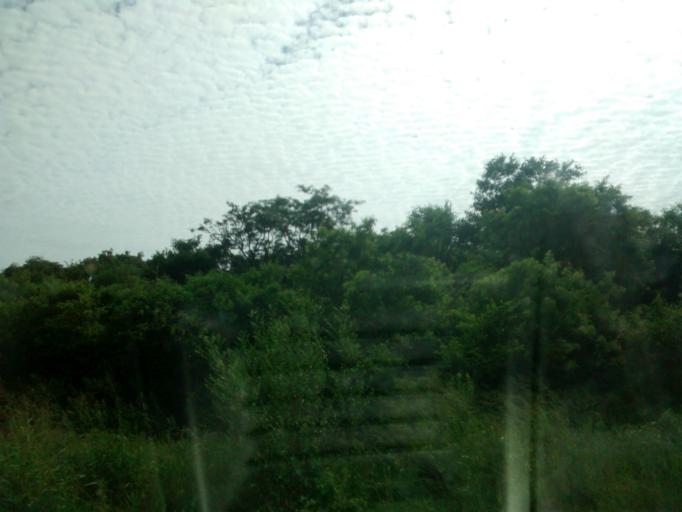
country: AR
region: Chaco
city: Fontana
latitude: -27.4049
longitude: -58.9897
